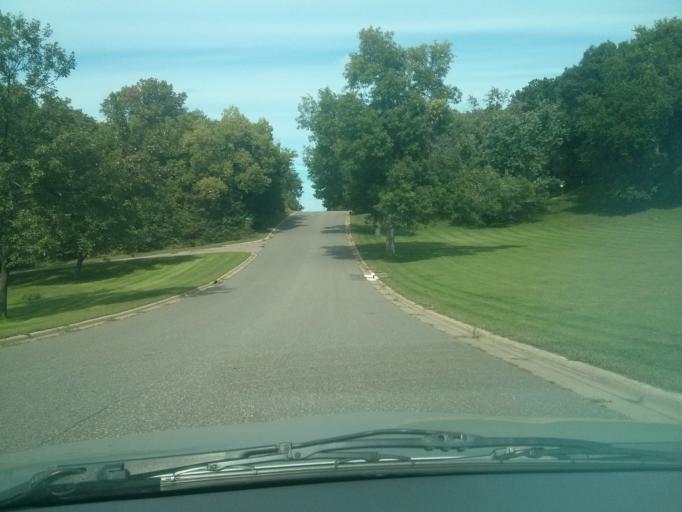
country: US
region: Wisconsin
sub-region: Saint Croix County
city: Hudson
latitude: 44.9771
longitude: -92.7438
